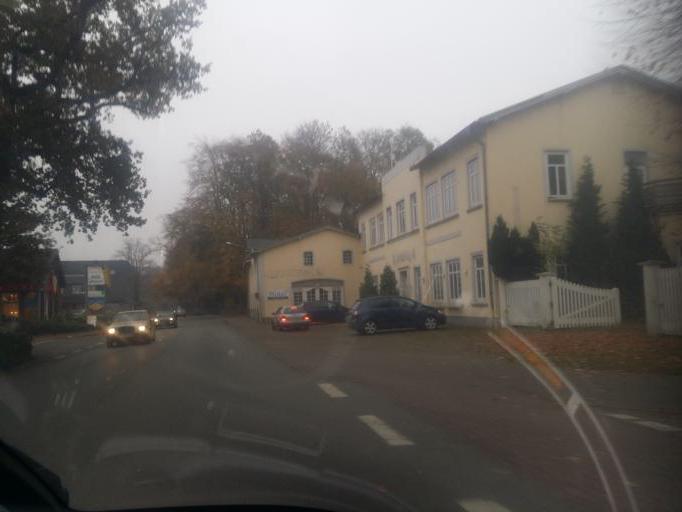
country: DE
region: Schleswig-Holstein
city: Satrup
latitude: 54.6931
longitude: 9.5975
